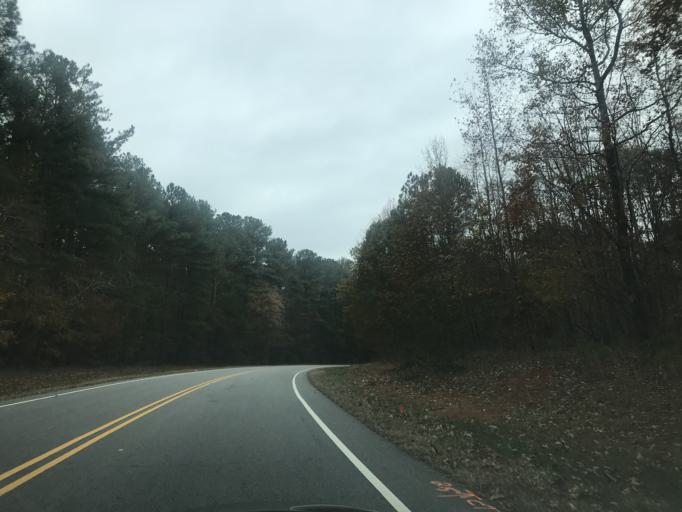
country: US
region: North Carolina
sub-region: Franklin County
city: Youngsville
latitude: 36.0075
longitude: -78.4904
